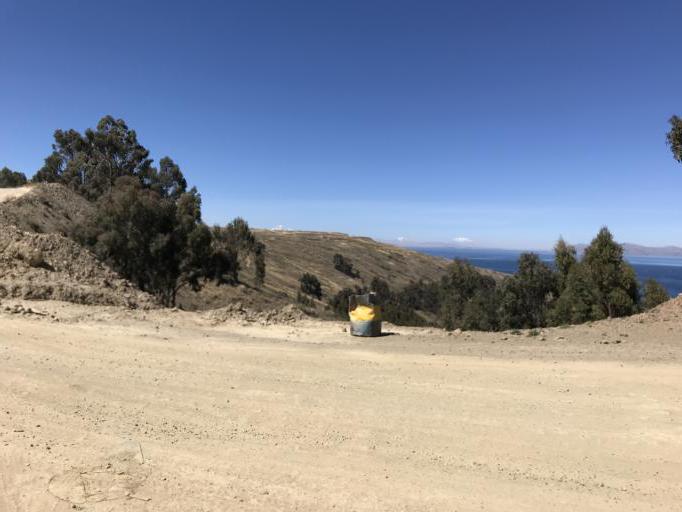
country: BO
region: La Paz
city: San Pablo
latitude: -16.1985
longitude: -68.8298
